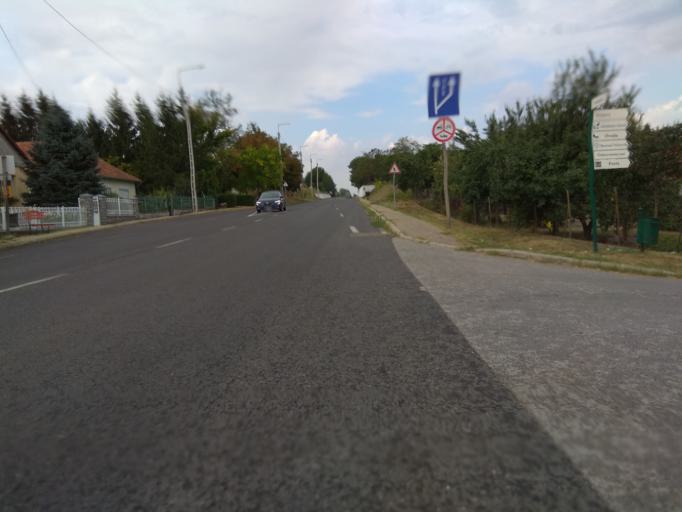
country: HU
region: Borsod-Abauj-Zemplen
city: Harsany
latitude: 47.9210
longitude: 20.7352
